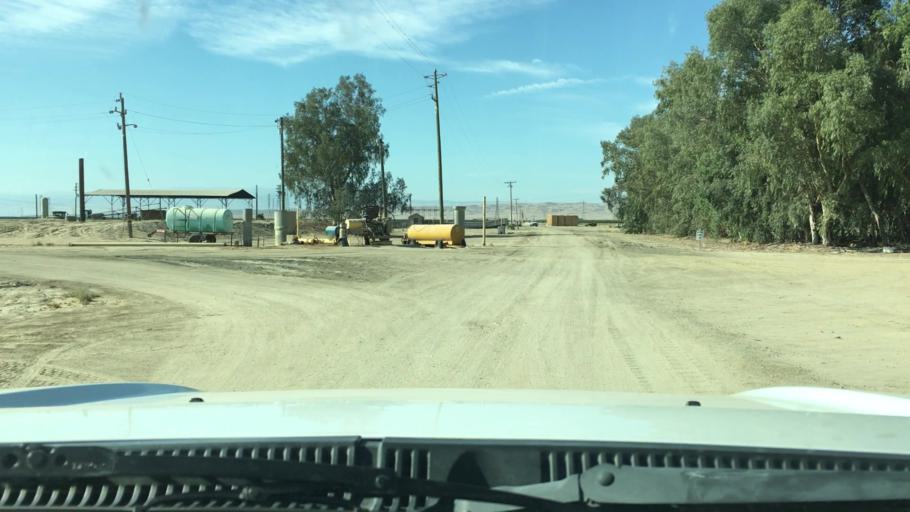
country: US
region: California
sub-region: Kern County
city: Buttonwillow
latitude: 35.3986
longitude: -119.4034
